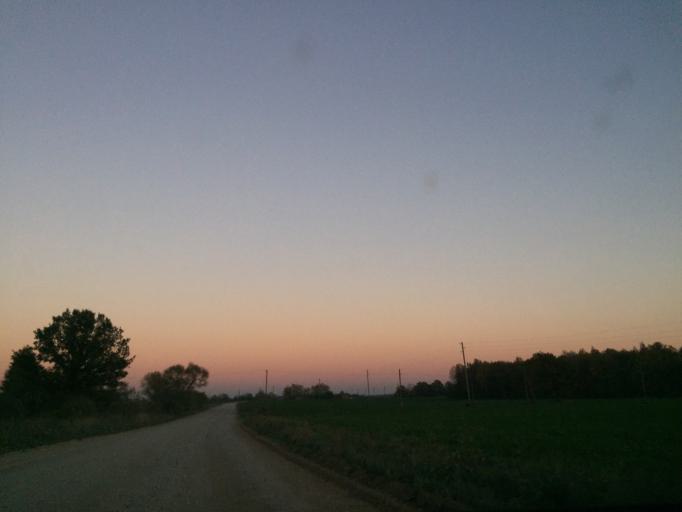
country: LT
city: Akmene
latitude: 56.3776
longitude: 22.7045
